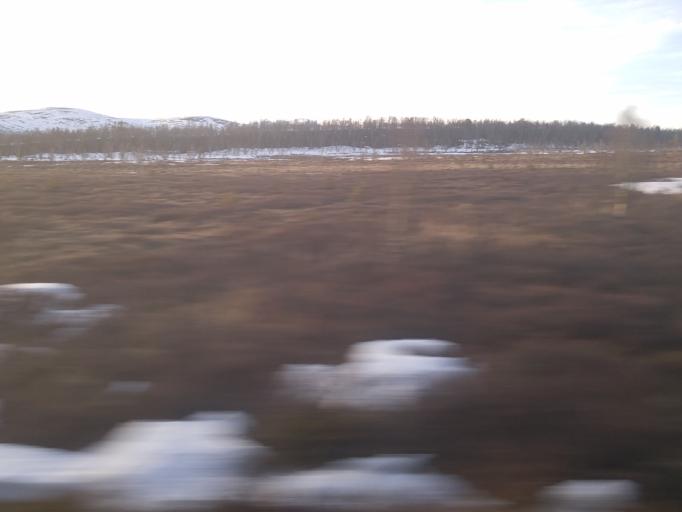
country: NO
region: Oppland
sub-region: Dovre
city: Dombas
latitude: 62.1034
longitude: 9.2357
